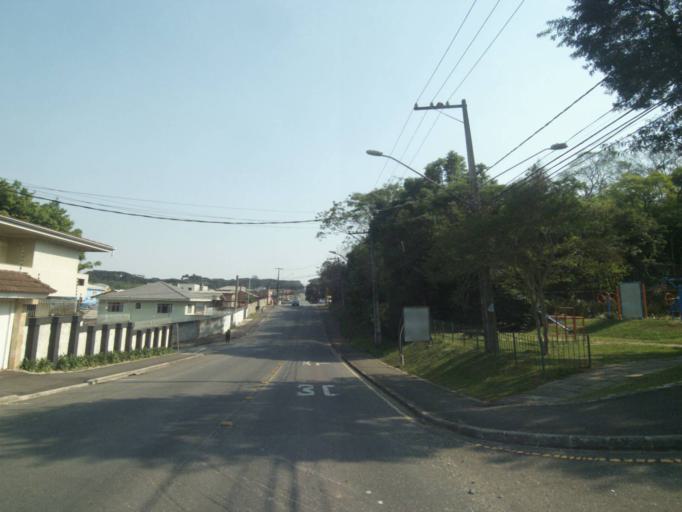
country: BR
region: Parana
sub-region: Sao Jose Dos Pinhais
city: Sao Jose dos Pinhais
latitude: -25.5180
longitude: -49.2493
